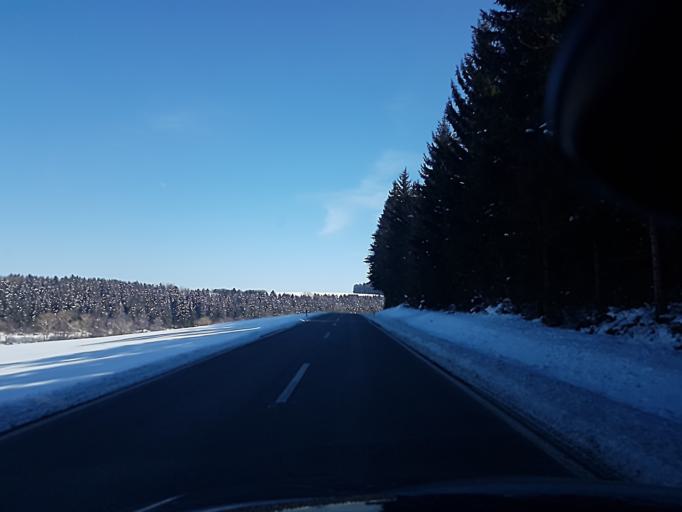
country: DE
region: Baden-Wuerttemberg
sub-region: Freiburg Region
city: Dunningen
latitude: 48.1720
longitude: 8.5007
